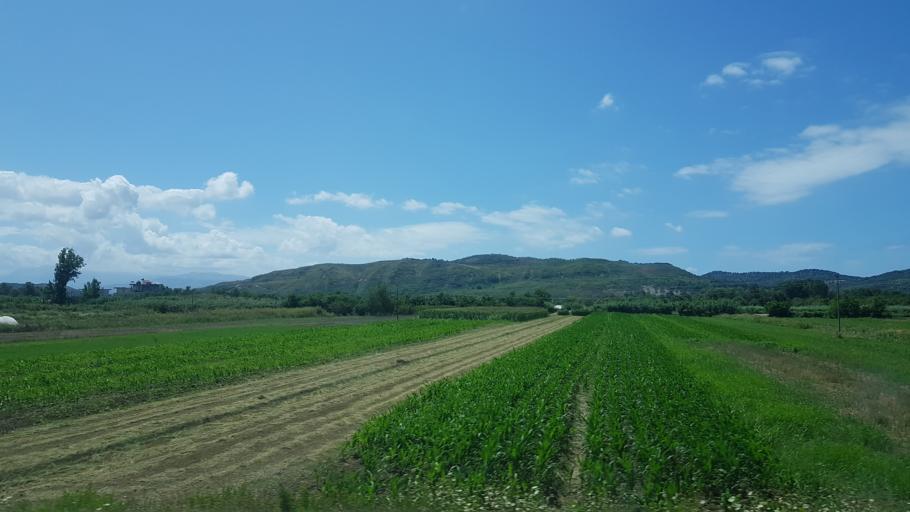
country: AL
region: Fier
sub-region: Rrethi i Fierit
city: Frakulla e Madhe
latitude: 40.6086
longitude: 19.5343
